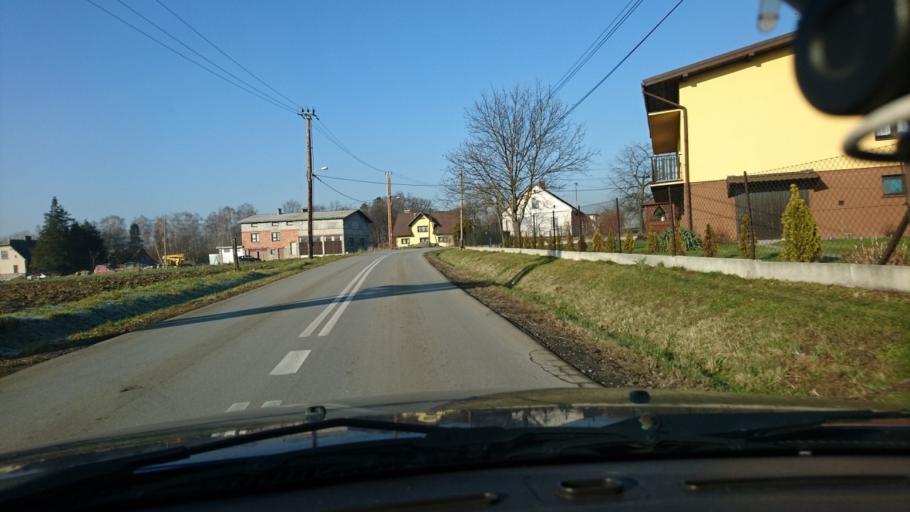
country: PL
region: Silesian Voivodeship
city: Janowice
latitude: 49.8784
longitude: 19.1032
